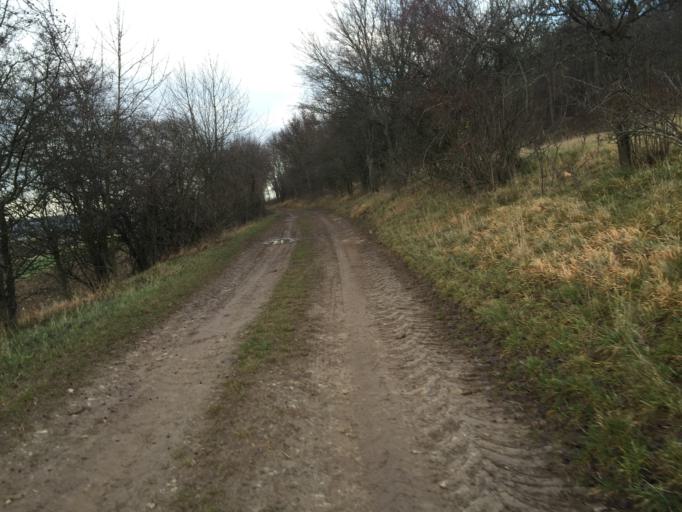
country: DE
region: Thuringia
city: Ranis
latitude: 50.6750
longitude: 11.5642
